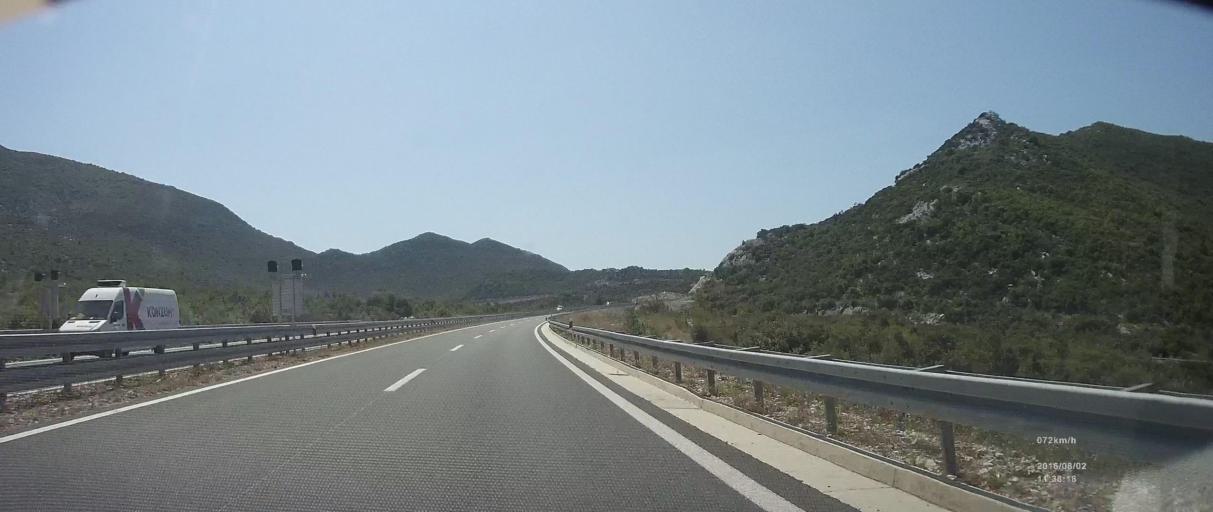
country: HR
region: Dubrovacko-Neretvanska
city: Komin
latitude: 43.0976
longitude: 17.4900
